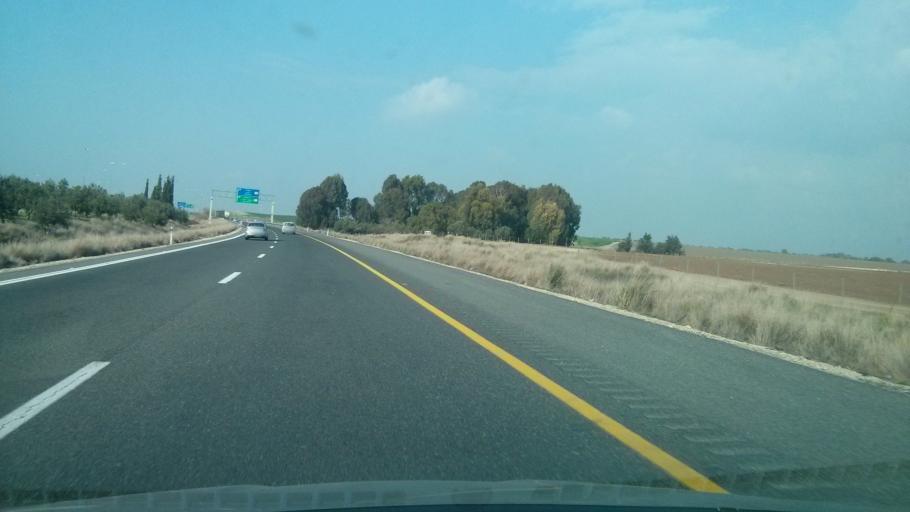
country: IL
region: Central District
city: Gedera
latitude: 31.7808
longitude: 34.8337
